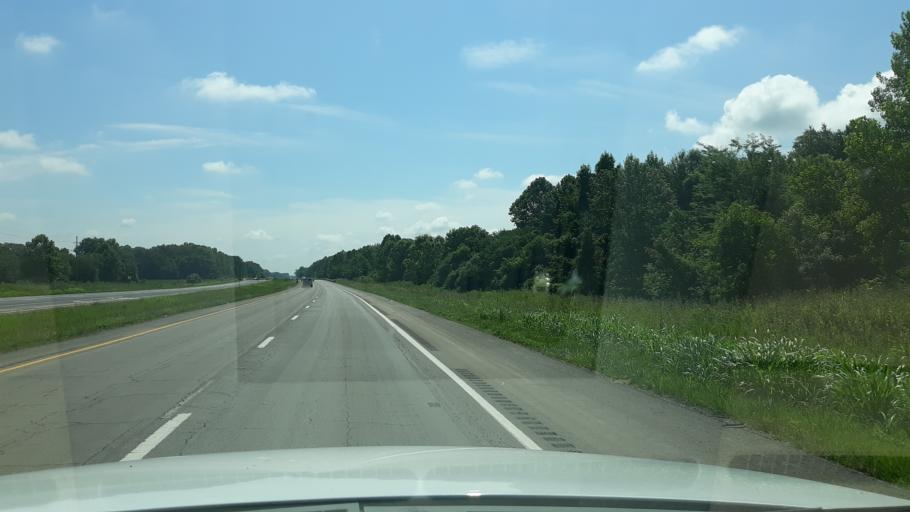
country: US
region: Illinois
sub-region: Saline County
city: Carrier Mills
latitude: 37.7333
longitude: -88.6731
